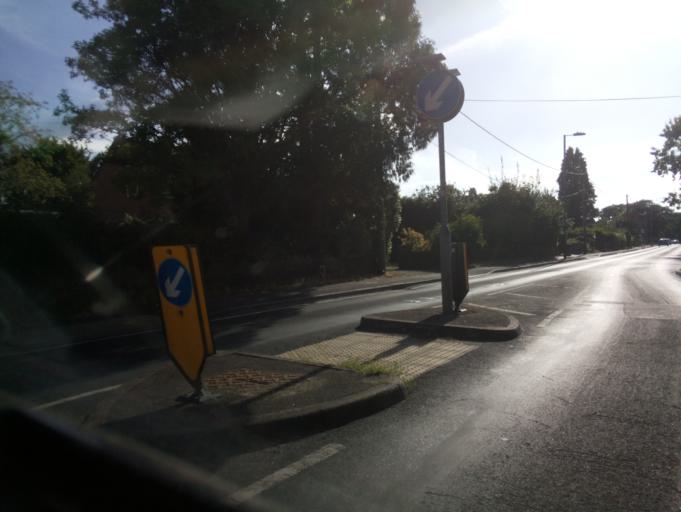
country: GB
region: England
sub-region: Hampshire
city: Romsey
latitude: 50.9877
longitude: -1.4744
